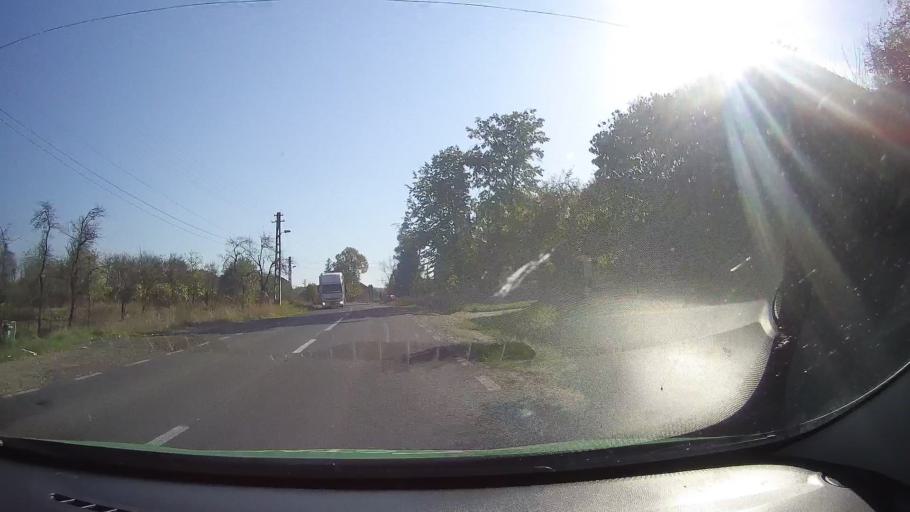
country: RO
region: Timis
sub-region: Comuna Curtea
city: Curtea
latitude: 45.8480
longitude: 22.3089
